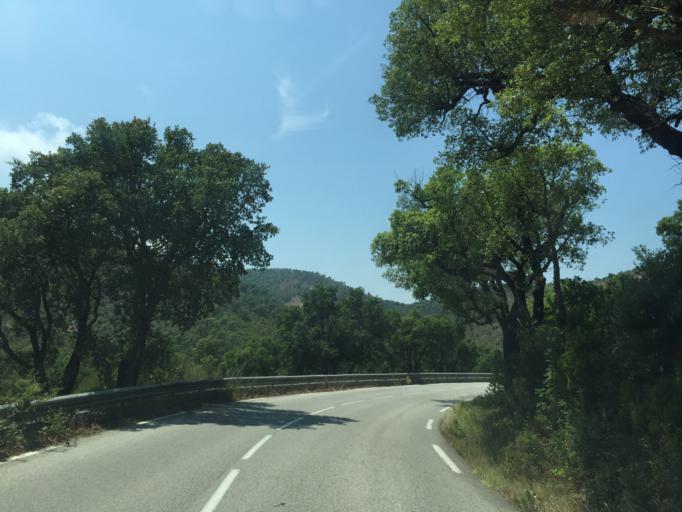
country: FR
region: Provence-Alpes-Cote d'Azur
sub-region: Departement du Var
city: Sainte-Maxime
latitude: 43.3677
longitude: 6.6747
